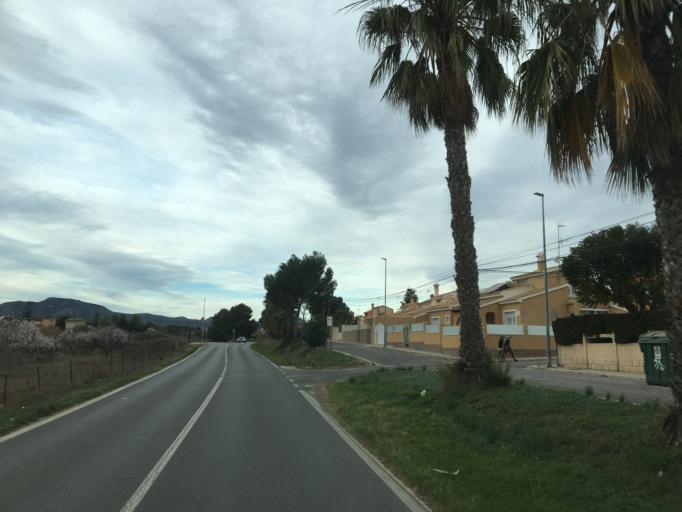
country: ES
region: Murcia
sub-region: Murcia
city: Cartagena
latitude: 37.6127
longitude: -1.0211
